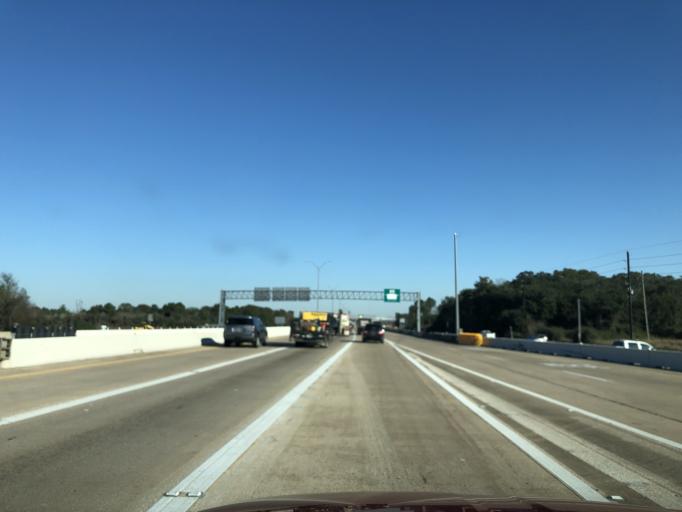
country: US
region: Texas
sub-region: Fort Bend County
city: Fresno
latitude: 29.5966
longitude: -95.4104
